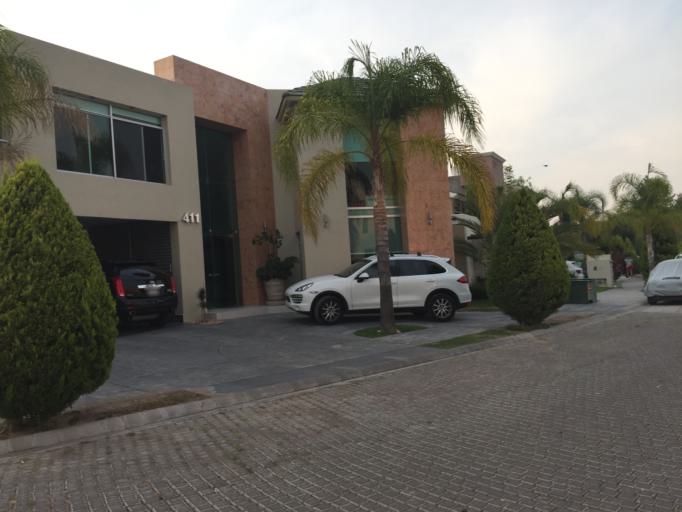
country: MX
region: Aguascalientes
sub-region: Aguascalientes
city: La Loma de los Negritos
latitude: 21.8480
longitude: -102.3558
